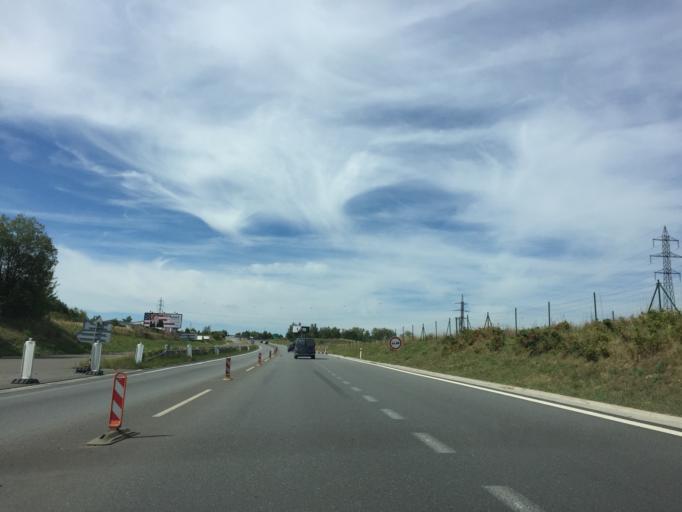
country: CZ
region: Jihocesky
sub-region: Okres Tabor
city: Sezimovo Usti
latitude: 49.4070
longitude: 14.7170
